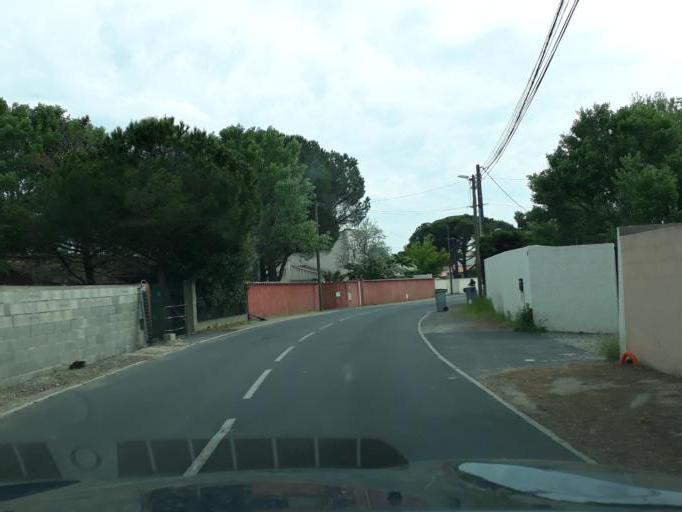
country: FR
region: Languedoc-Roussillon
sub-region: Departement de l'Herault
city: Agde
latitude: 43.2807
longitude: 3.4686
